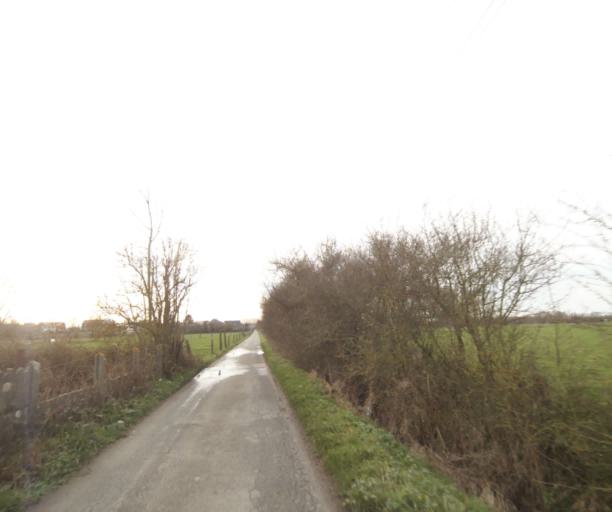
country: BE
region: Wallonia
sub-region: Province du Hainaut
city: Peruwelz
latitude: 50.4919
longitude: 3.5773
